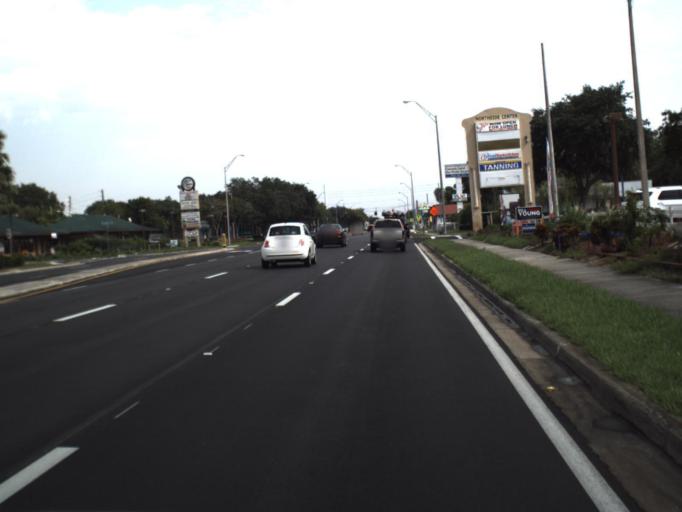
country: US
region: Florida
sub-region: Pinellas County
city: Lealman
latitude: 27.8253
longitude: -82.6385
